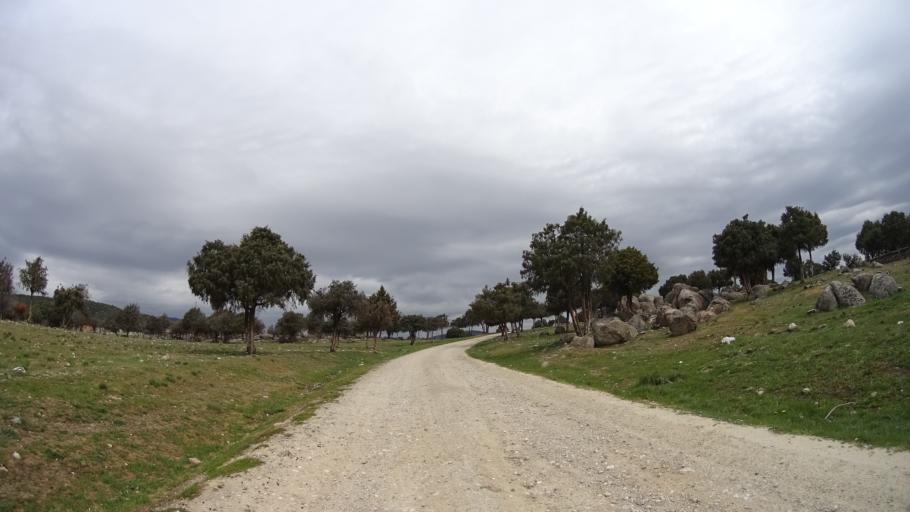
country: ES
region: Madrid
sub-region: Provincia de Madrid
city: Hoyo de Manzanares
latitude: 40.6054
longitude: -3.8776
